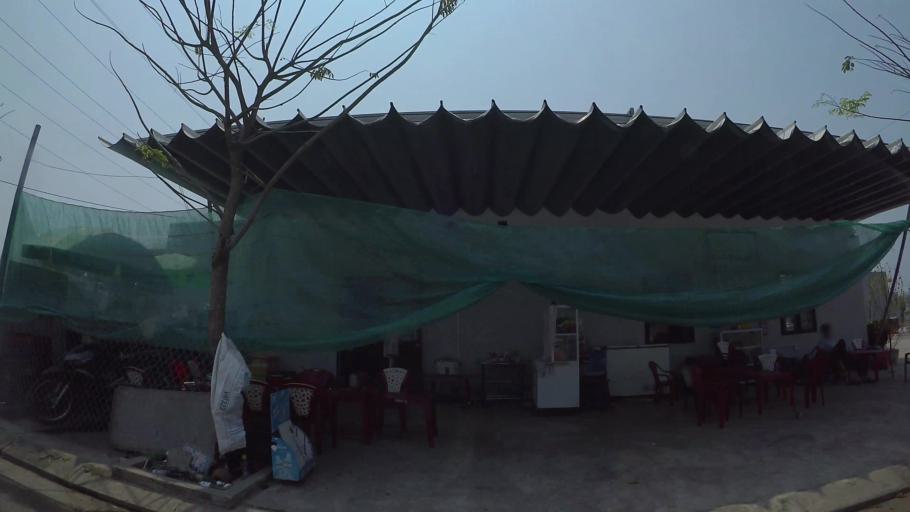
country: VN
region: Da Nang
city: Ngu Hanh Son
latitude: 16.0175
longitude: 108.2287
